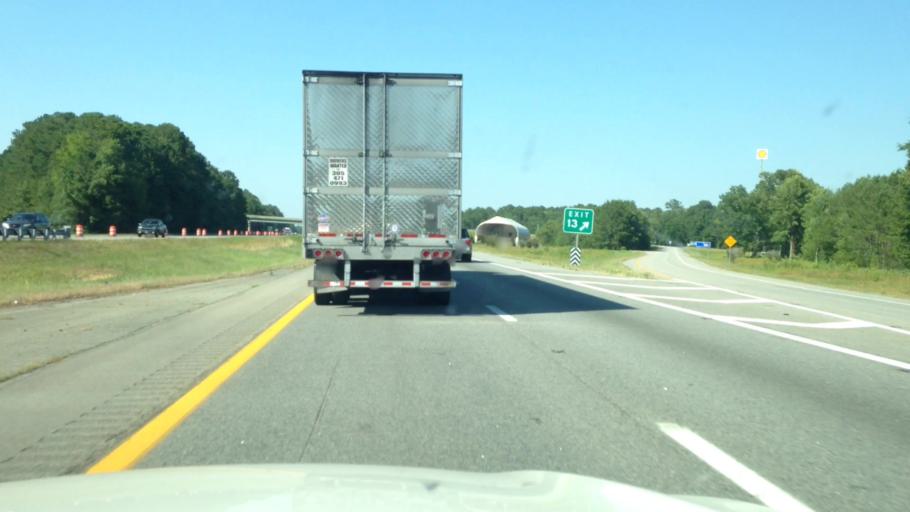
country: US
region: Virginia
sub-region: City of Emporia
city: Emporia
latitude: 36.7299
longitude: -77.5239
